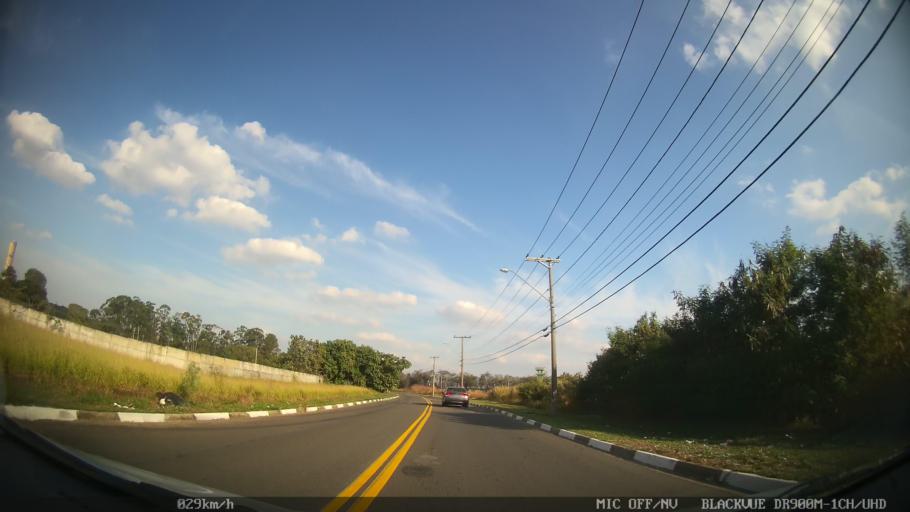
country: BR
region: Sao Paulo
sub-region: Hortolandia
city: Hortolandia
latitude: -22.8725
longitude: -47.1556
